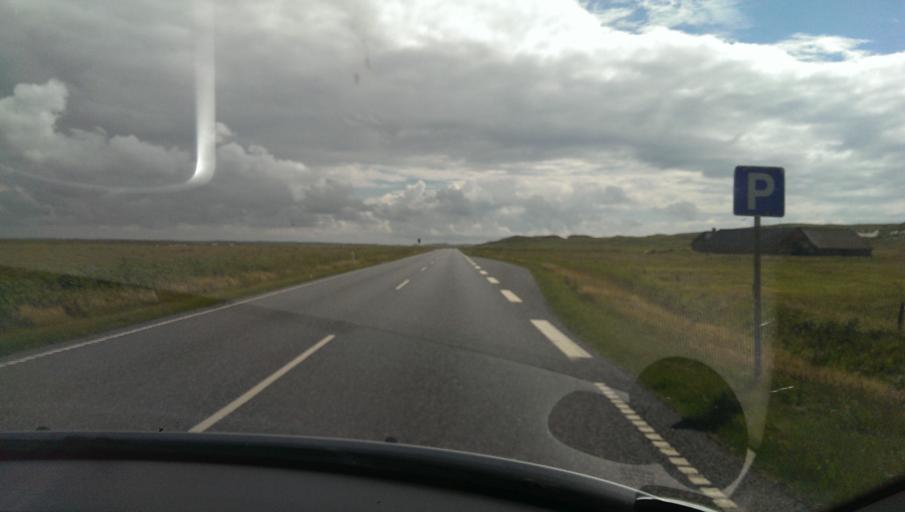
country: DK
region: Central Jutland
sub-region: Ringkobing-Skjern Kommune
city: Ringkobing
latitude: 56.2051
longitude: 8.1322
